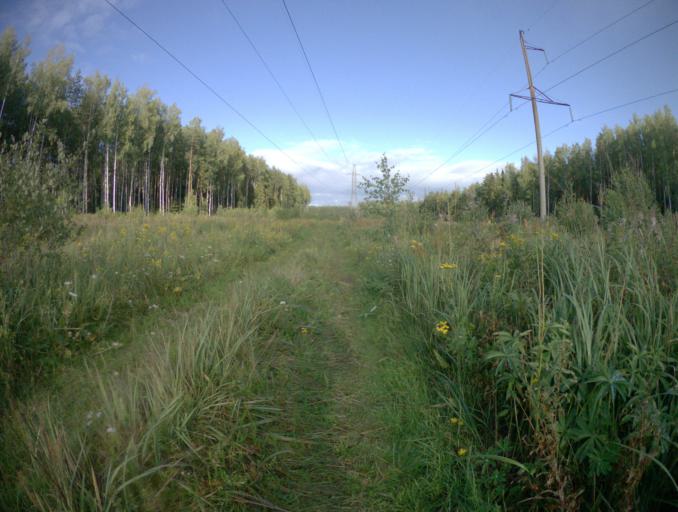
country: RU
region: Vladimir
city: Raduzhnyy
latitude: 56.0136
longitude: 40.2838
